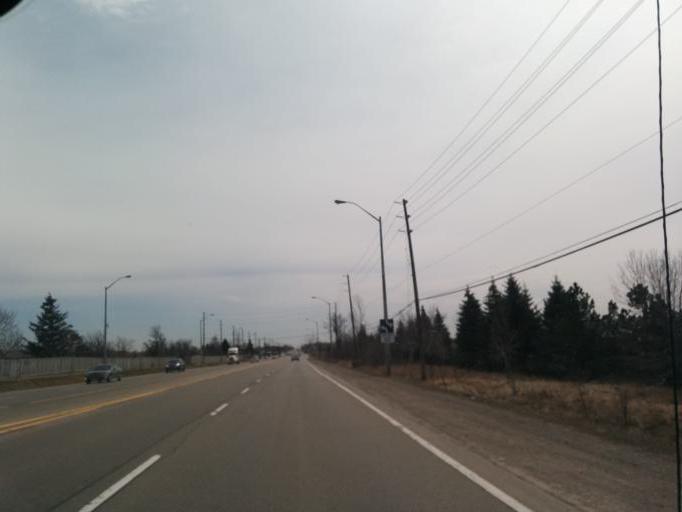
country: CA
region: Ontario
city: Brampton
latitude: 43.7209
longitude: -79.8075
